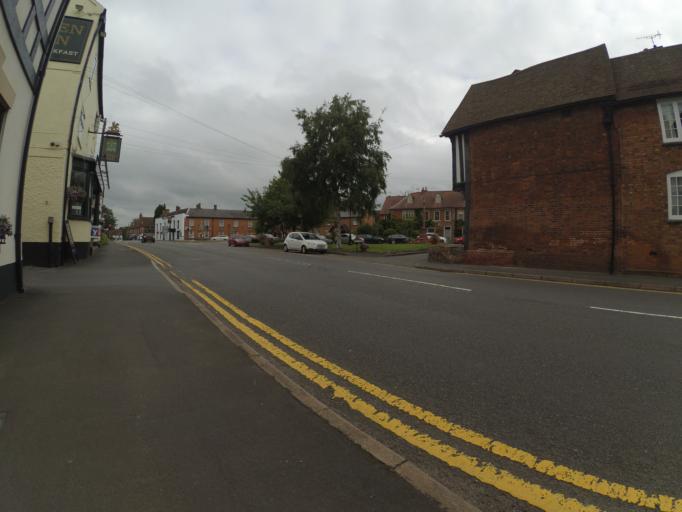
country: GB
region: England
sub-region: Warwickshire
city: Dunchurch
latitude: 52.3367
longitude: -1.2890
